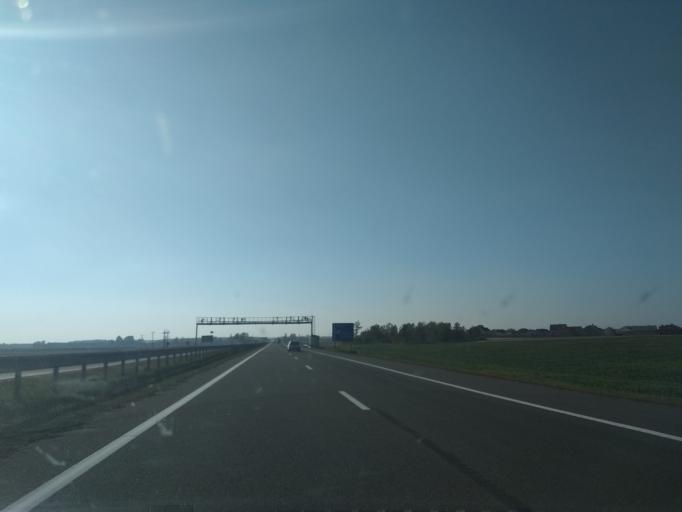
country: BY
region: Brest
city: Zhabinka
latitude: 52.1202
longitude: 23.8692
